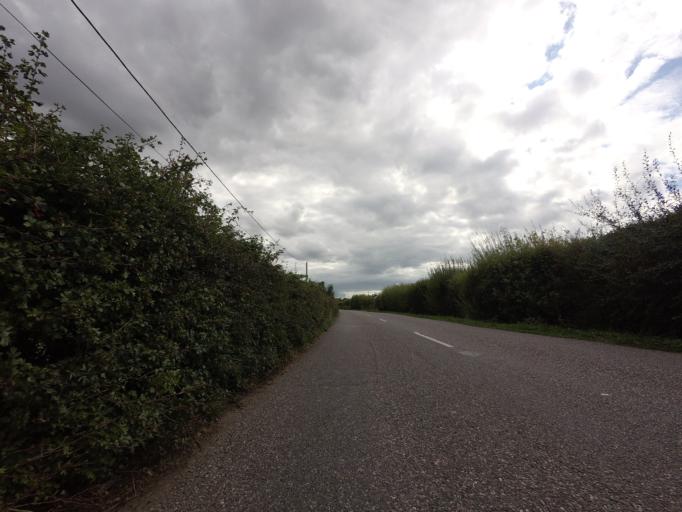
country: GB
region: England
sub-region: Kent
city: Marden
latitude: 51.1649
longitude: 0.4489
